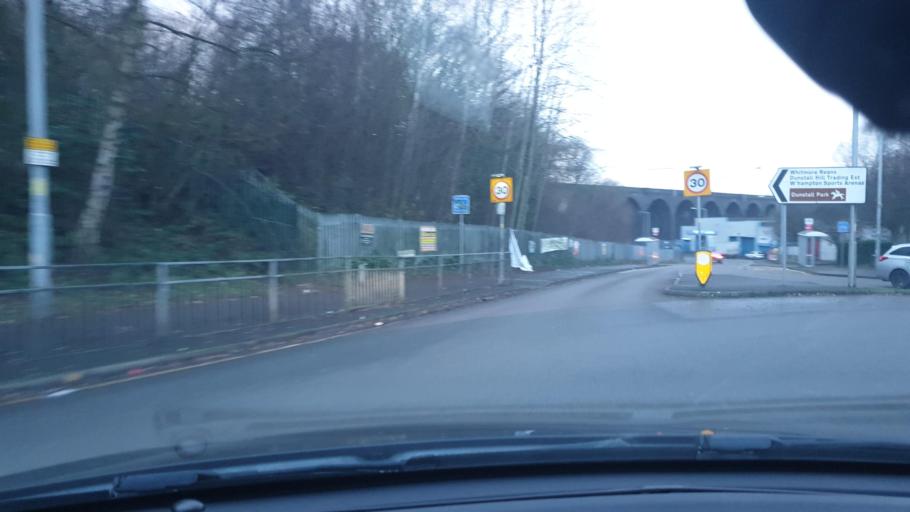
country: GB
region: England
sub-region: Wolverhampton
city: Wolverhampton
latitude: 52.6015
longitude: -2.1302
